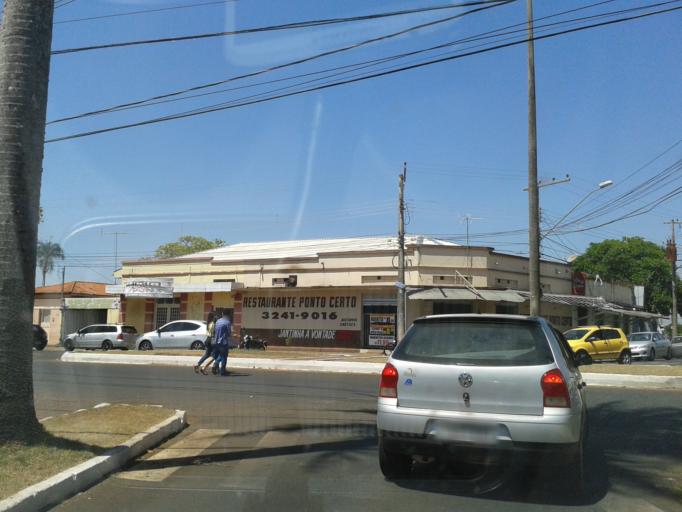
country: BR
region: Minas Gerais
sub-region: Araguari
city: Araguari
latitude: -18.6593
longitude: -48.1861
